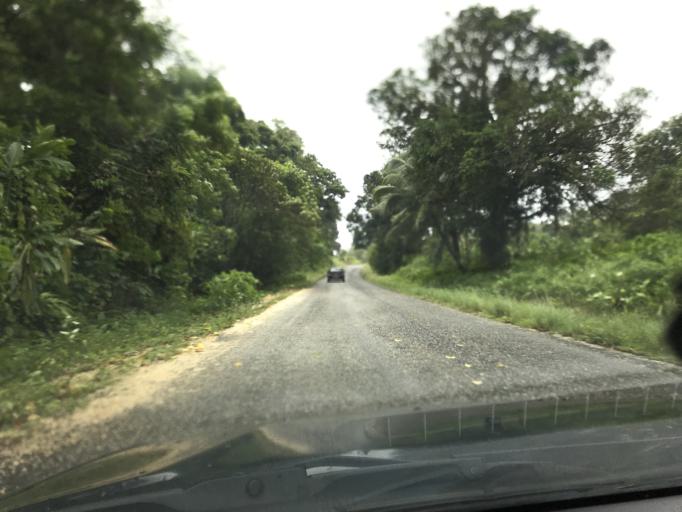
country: SB
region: Western Province
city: Gizo
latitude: -8.2477
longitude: 157.2353
